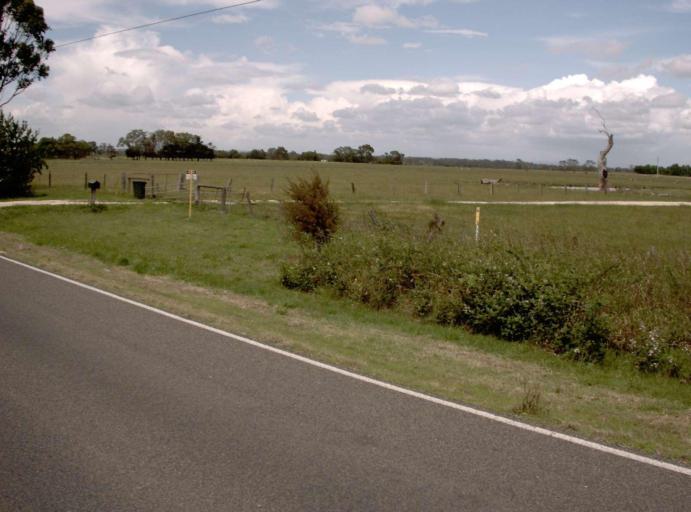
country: AU
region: Victoria
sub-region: Wellington
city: Sale
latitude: -38.0228
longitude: 147.0116
